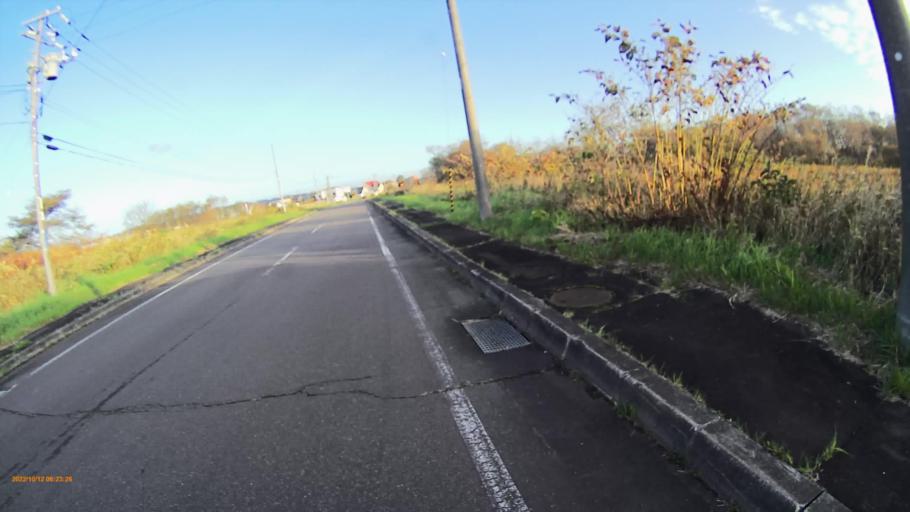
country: JP
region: Hokkaido
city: Kushiro
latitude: 42.8890
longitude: 143.9368
